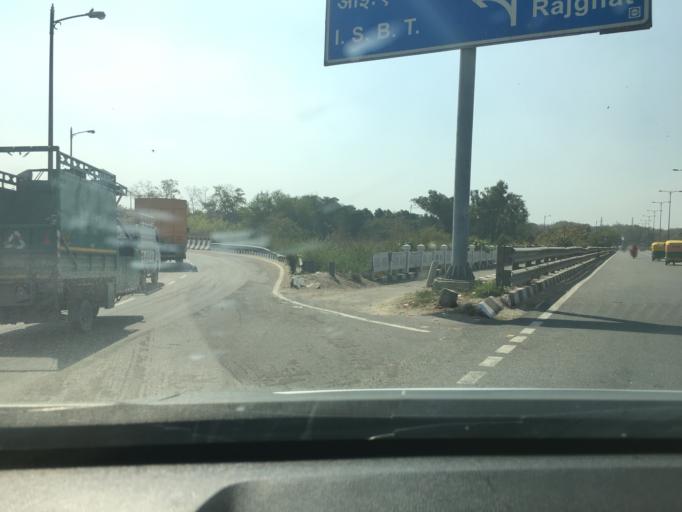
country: IN
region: NCT
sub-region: North Delhi
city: Delhi
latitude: 28.6512
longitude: 77.2508
